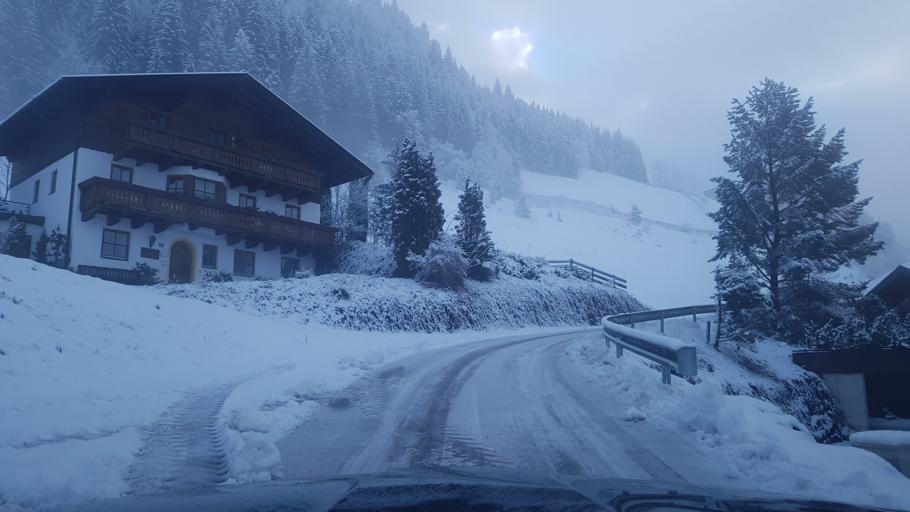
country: AT
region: Salzburg
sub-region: Politischer Bezirk Sankt Johann im Pongau
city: Sankt Johann im Pongau
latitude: 47.3256
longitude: 13.2053
